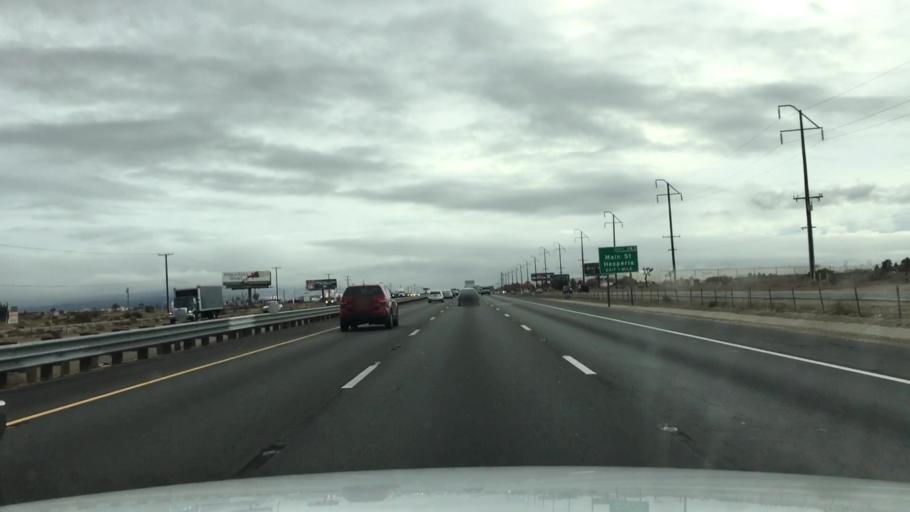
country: US
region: California
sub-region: San Bernardino County
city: Oak Hills
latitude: 34.4401
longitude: -117.3691
